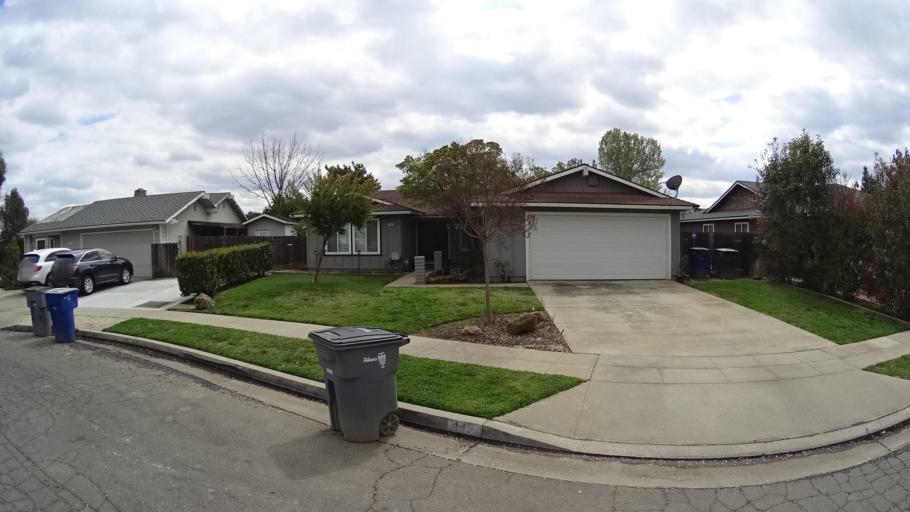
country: US
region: California
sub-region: Fresno County
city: Fresno
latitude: 36.8341
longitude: -119.8005
